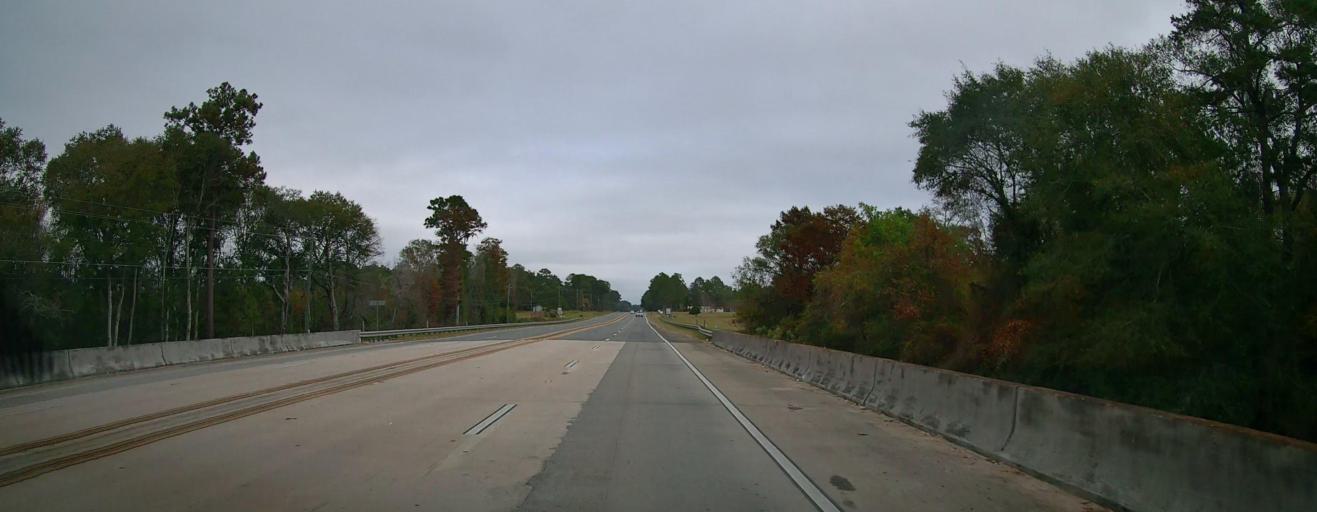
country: US
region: Georgia
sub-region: Tift County
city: Omega
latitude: 31.2975
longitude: -83.6579
